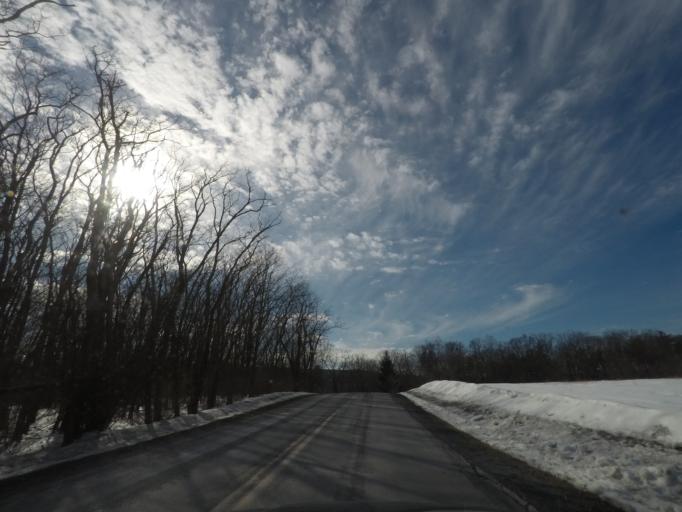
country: US
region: New York
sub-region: Albany County
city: Voorheesville
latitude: 42.6592
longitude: -73.9646
